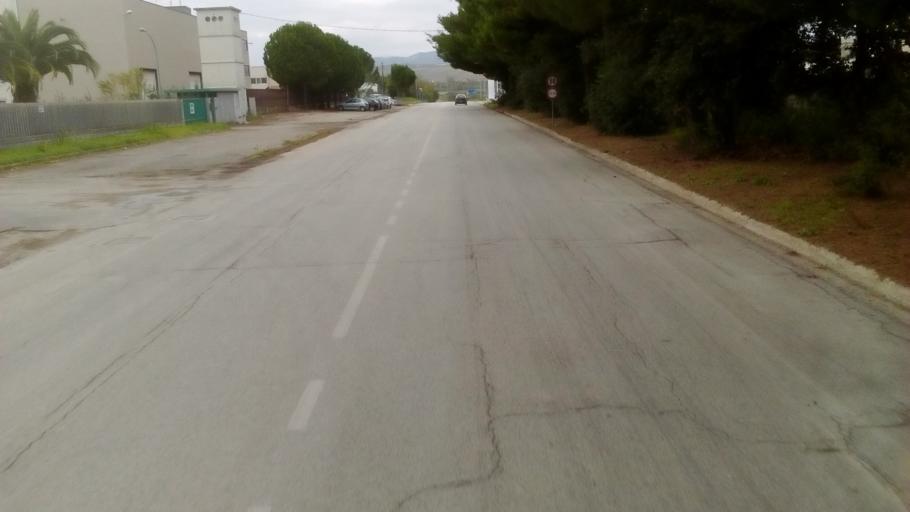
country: IT
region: Abruzzo
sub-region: Provincia di Chieti
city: San Salvo
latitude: 42.0364
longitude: 14.7452
